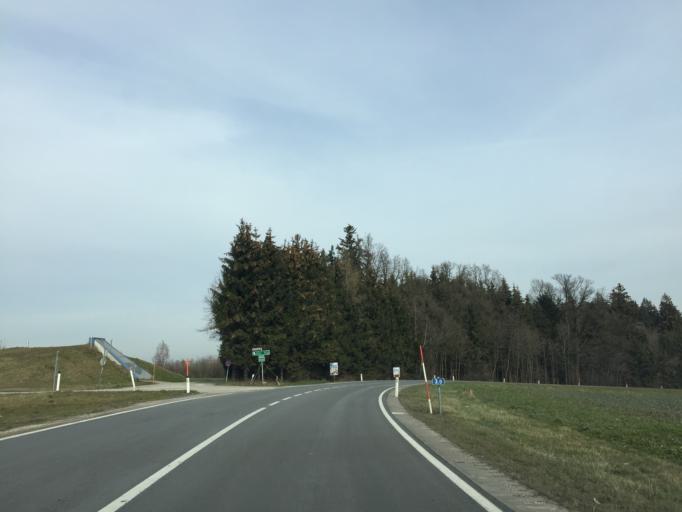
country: AT
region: Upper Austria
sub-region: Politischer Bezirk Ried im Innkreis
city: Ried im Innkreis
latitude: 48.2352
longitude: 13.5067
